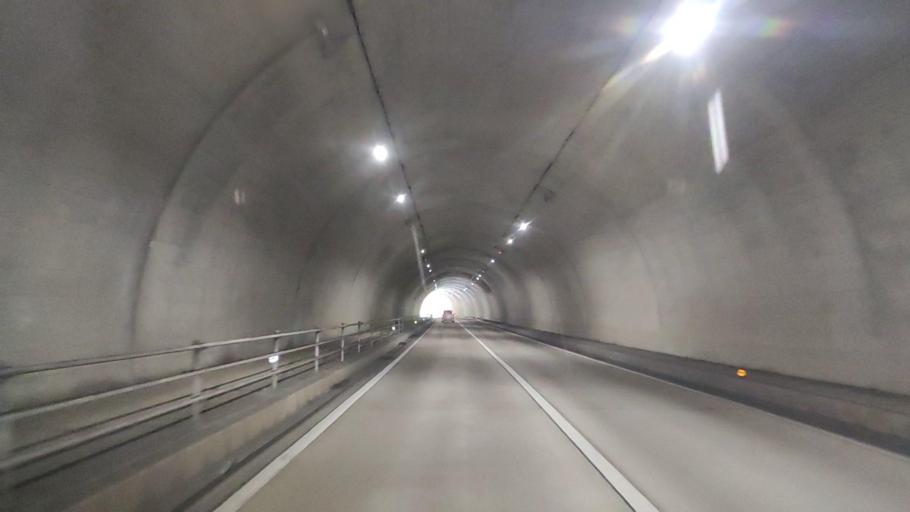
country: JP
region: Gifu
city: Godo
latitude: 35.5598
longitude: 136.6405
